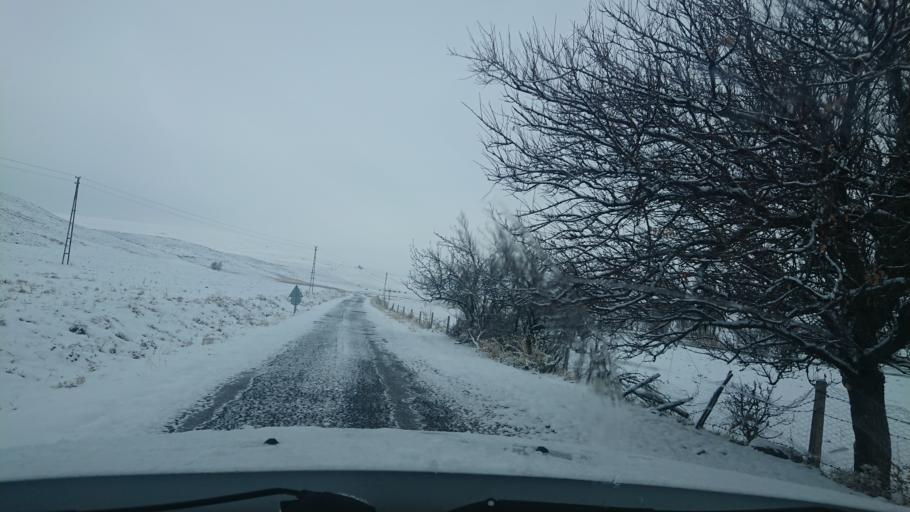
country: TR
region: Aksaray
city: Acipinar
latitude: 38.6783
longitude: 33.8667
